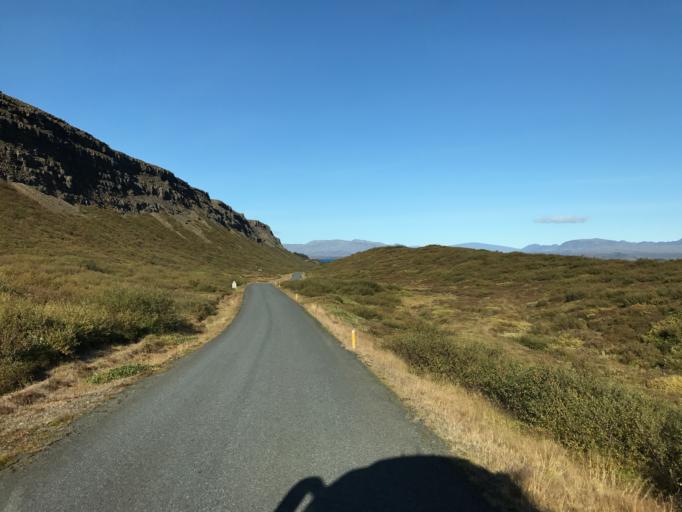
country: IS
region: South
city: Hveragerdi
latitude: 64.1623
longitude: -21.2449
